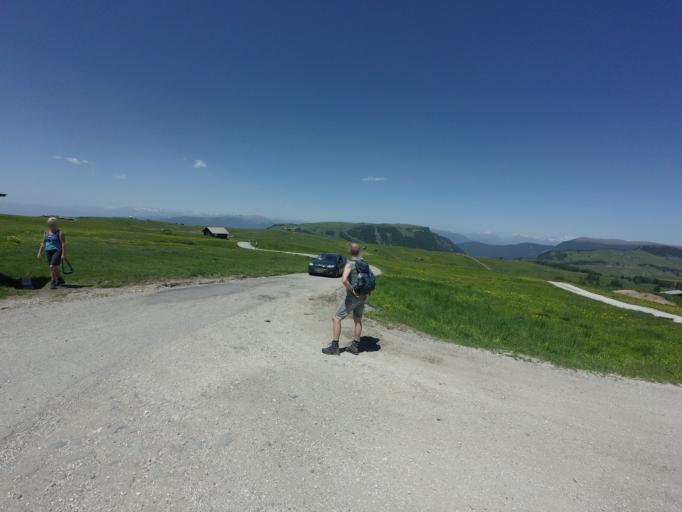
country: IT
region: Trentino-Alto Adige
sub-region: Bolzano
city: Ortisei
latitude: 46.5228
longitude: 11.6371
